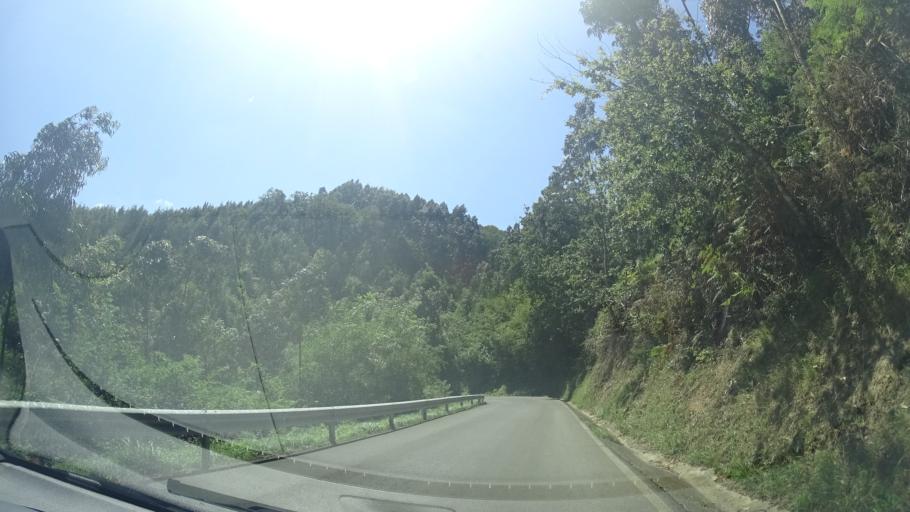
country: ES
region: Asturias
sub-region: Province of Asturias
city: Ribadesella
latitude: 43.4469
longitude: -5.0755
